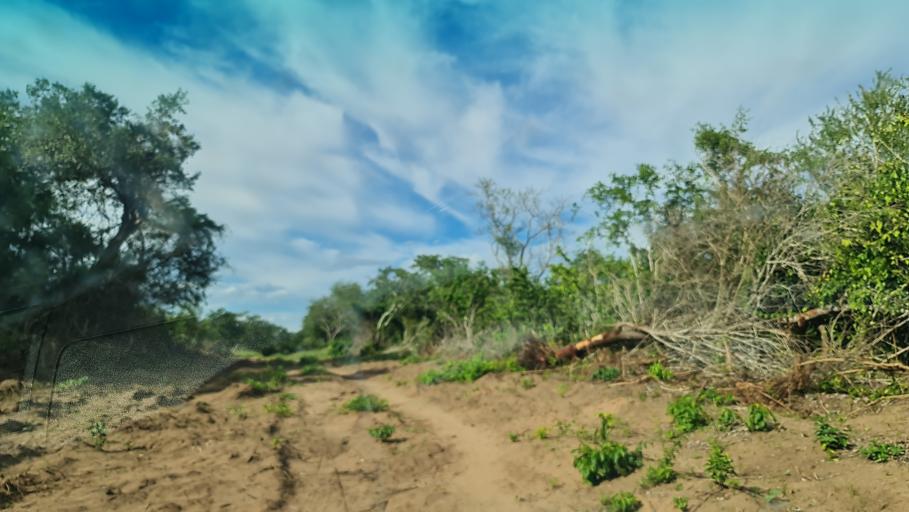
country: MZ
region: Nampula
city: Ilha de Mocambique
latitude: -15.5027
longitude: 40.1577
